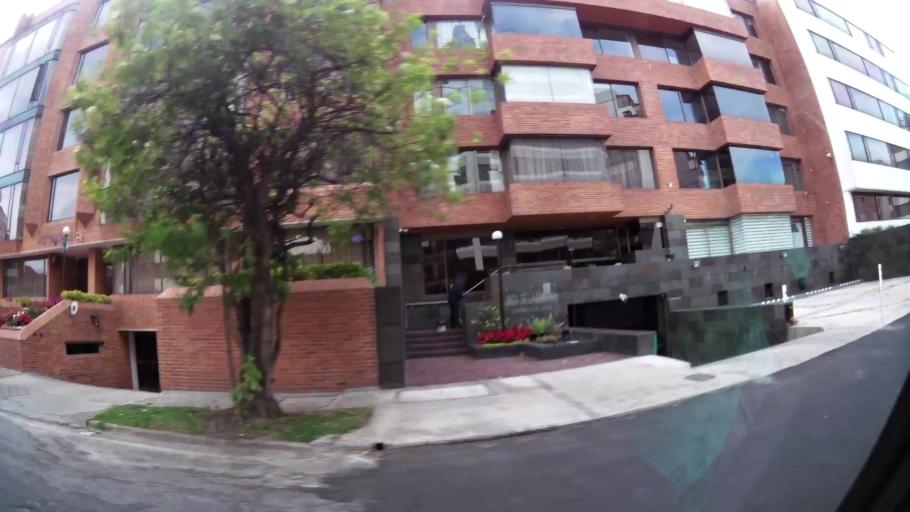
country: CO
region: Bogota D.C.
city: Barrio San Luis
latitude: 4.6979
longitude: -74.0351
